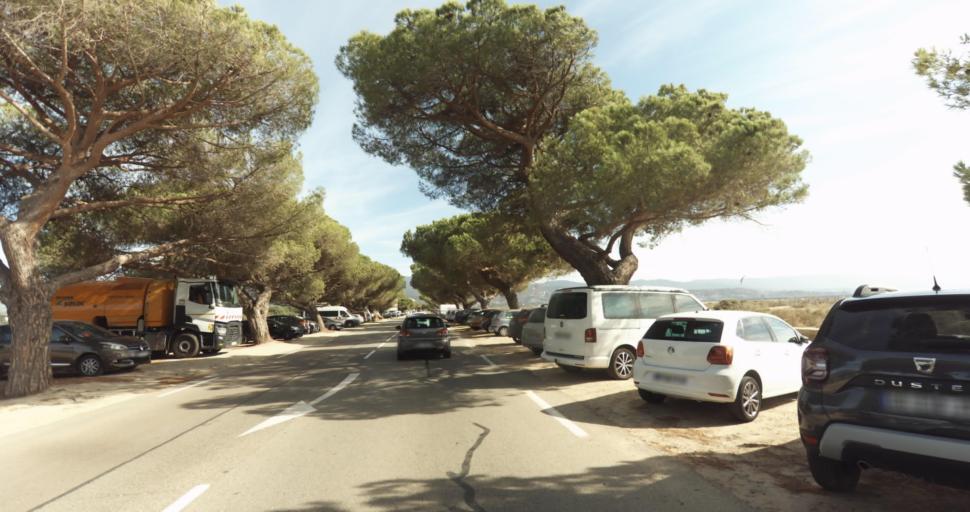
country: FR
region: Corsica
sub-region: Departement de la Corse-du-Sud
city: Ajaccio
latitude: 41.9233
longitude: 8.7846
